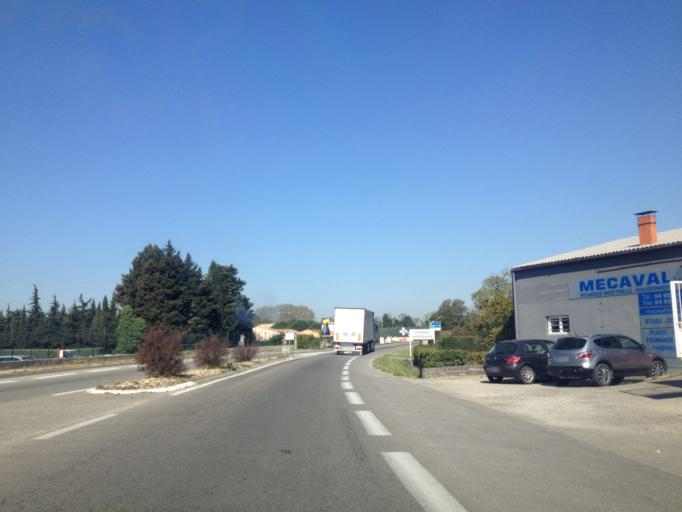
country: FR
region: Provence-Alpes-Cote d'Azur
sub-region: Departement du Vaucluse
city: Sarrians
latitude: 44.0868
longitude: 4.9694
